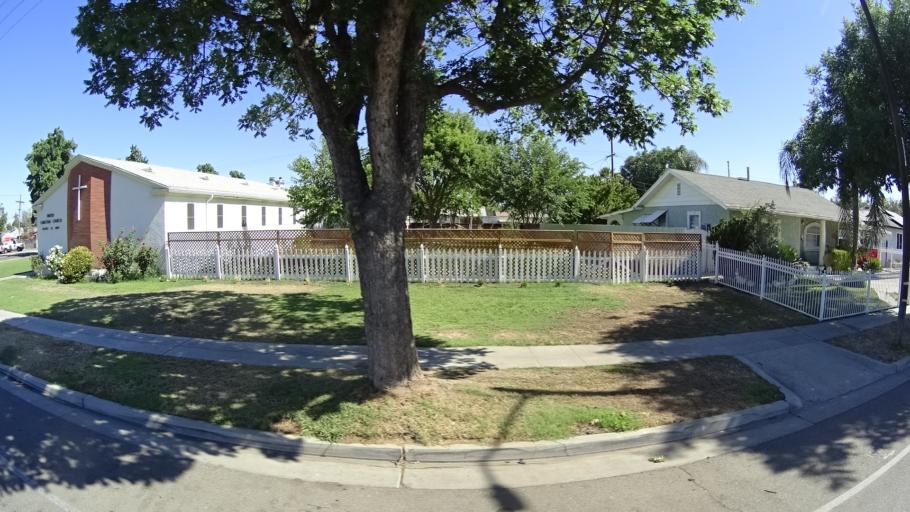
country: US
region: California
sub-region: Fresno County
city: Fresno
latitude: 36.7794
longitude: -119.8236
